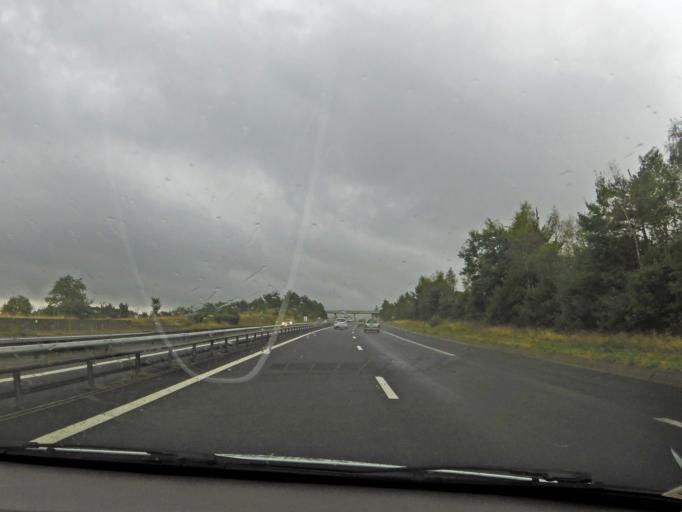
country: FR
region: Auvergne
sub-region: Departement du Cantal
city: Saint-Flour
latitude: 44.9647
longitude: 3.1921
